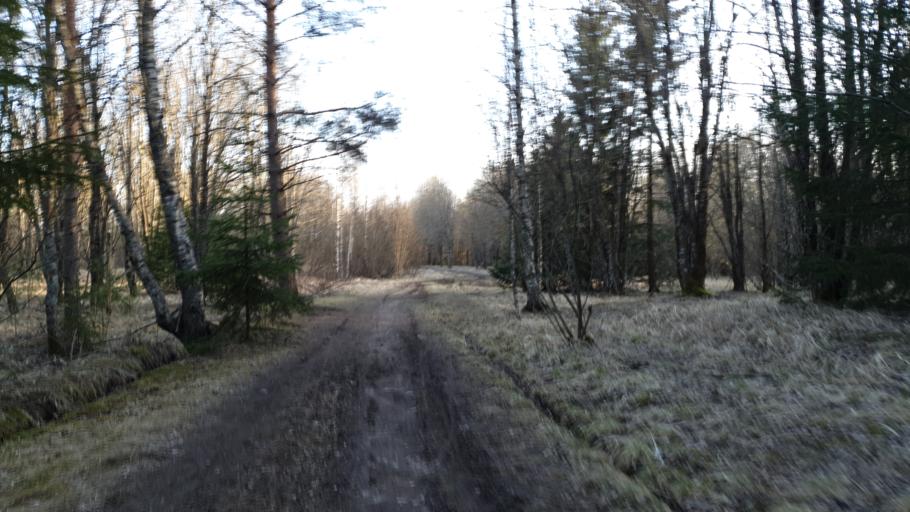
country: FI
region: Uusimaa
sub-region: Helsinki
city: Nurmijaervi
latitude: 60.3369
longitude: 24.8444
